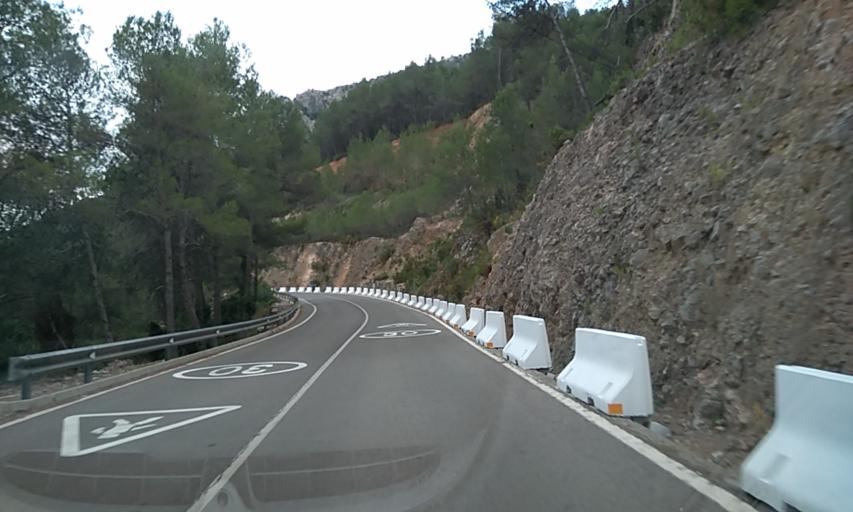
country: ES
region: Valencia
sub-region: Provincia de Castello
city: Montanejos
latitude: 40.0751
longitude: -0.5383
